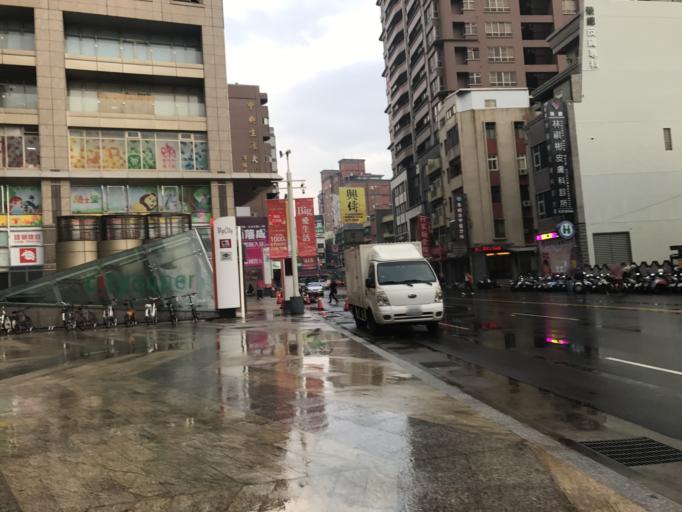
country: TW
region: Taiwan
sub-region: Hsinchu
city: Hsinchu
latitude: 24.8095
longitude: 120.9759
